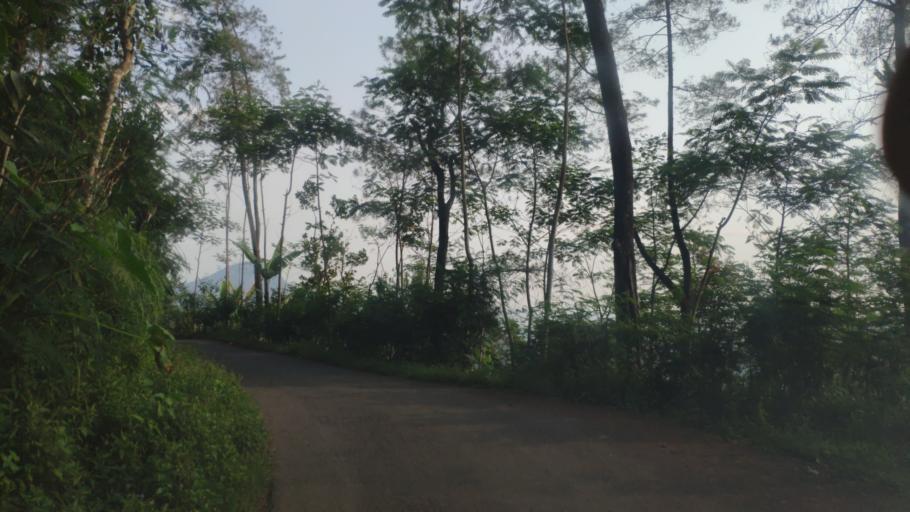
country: ID
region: Central Java
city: Buaran
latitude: -7.2537
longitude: 109.6737
